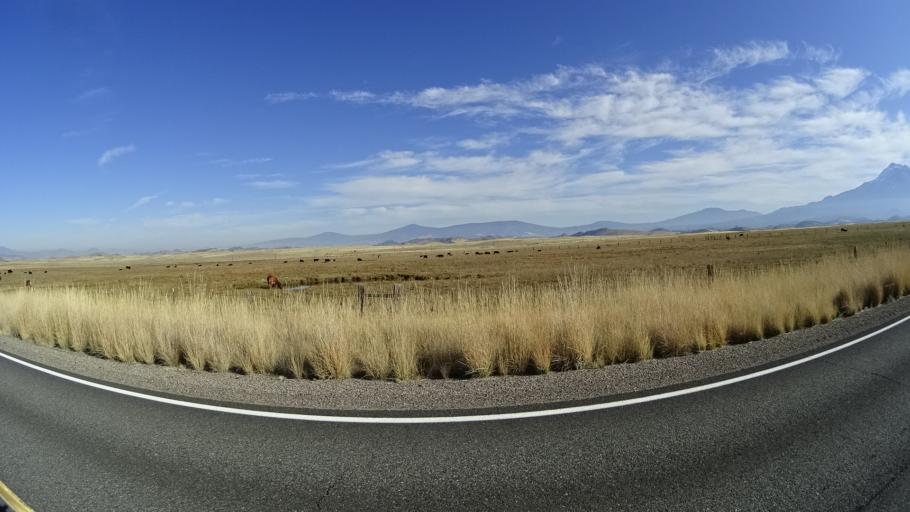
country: US
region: California
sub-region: Siskiyou County
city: Weed
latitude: 41.4882
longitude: -122.5037
